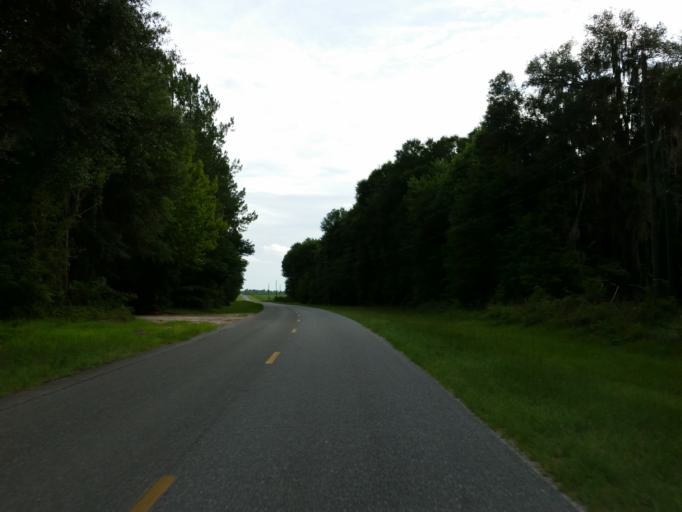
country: US
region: Florida
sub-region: Hamilton County
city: Jasper
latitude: 30.4796
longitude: -83.1400
